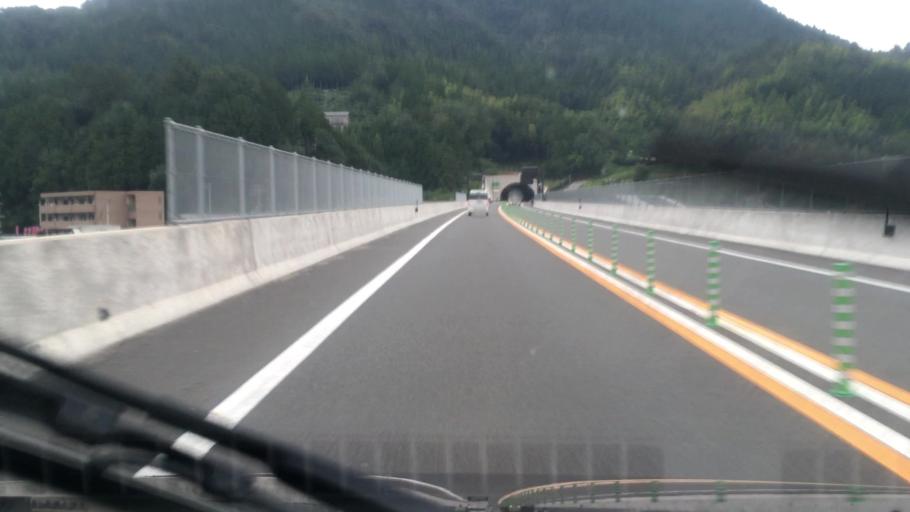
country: JP
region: Hyogo
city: Toyooka
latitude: 35.3936
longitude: 134.7450
